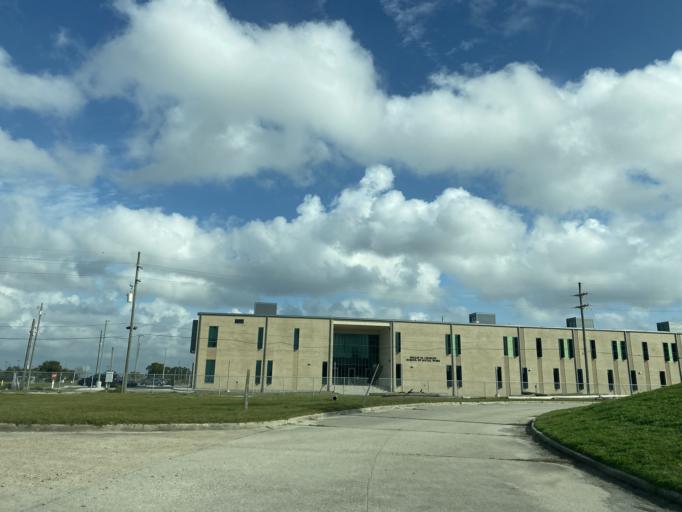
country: US
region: Louisiana
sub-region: Orleans Parish
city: New Orleans
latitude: 30.0315
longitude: -90.0468
